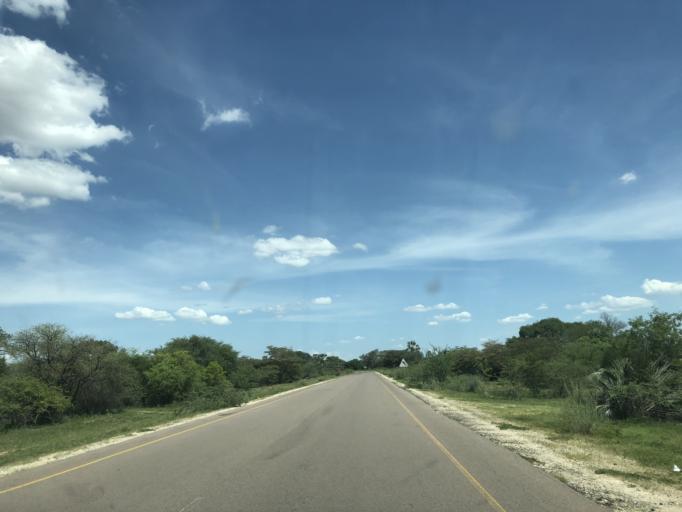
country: AO
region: Cunene
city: Ondjiva
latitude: -16.8861
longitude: 15.4912
